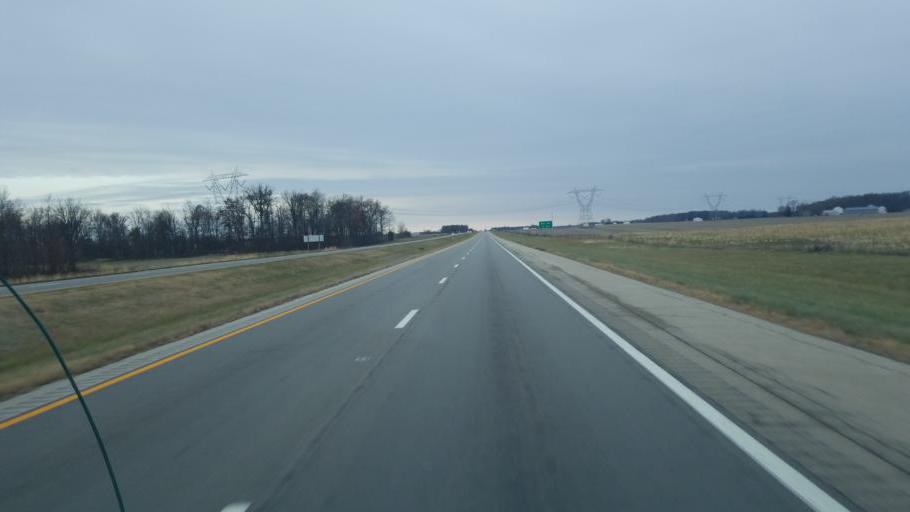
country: US
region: Ohio
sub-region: Auglaize County
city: Wapakoneta
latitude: 40.5640
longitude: -84.2664
